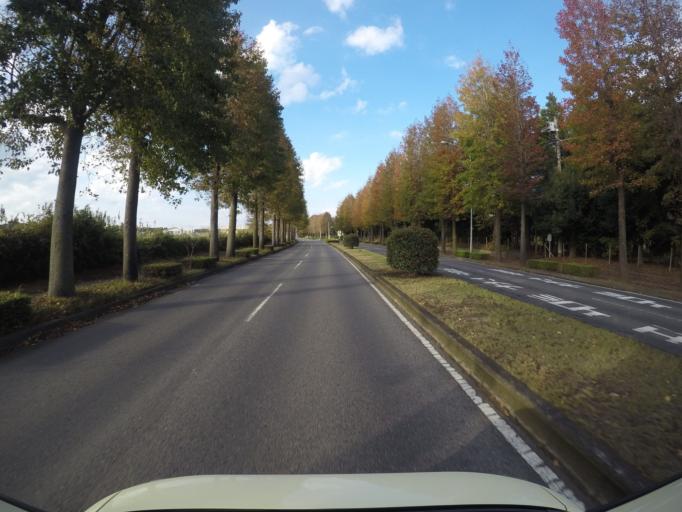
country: JP
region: Ibaraki
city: Naka
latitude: 36.0599
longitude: 140.1024
